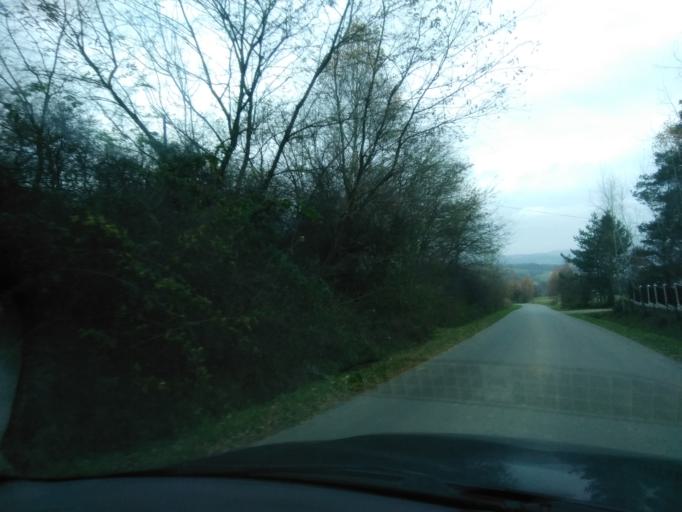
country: PL
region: Subcarpathian Voivodeship
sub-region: Powiat strzyzowski
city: Wysoka Strzyzowska
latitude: 49.8348
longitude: 21.7760
